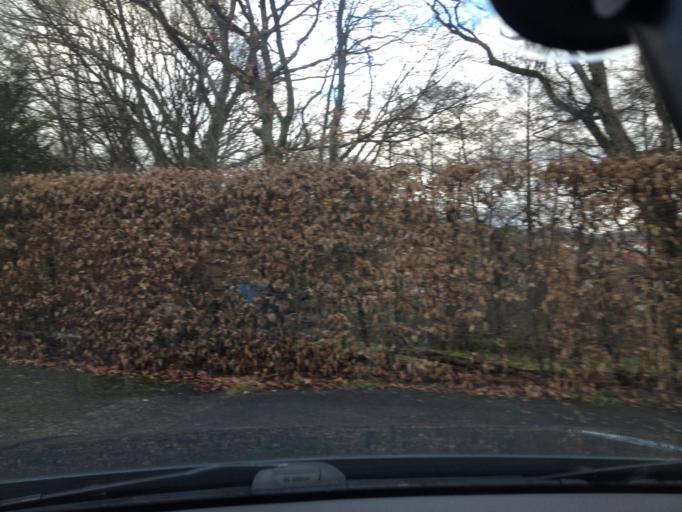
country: DE
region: Saarland
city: Namborn
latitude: 49.5065
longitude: 7.1559
